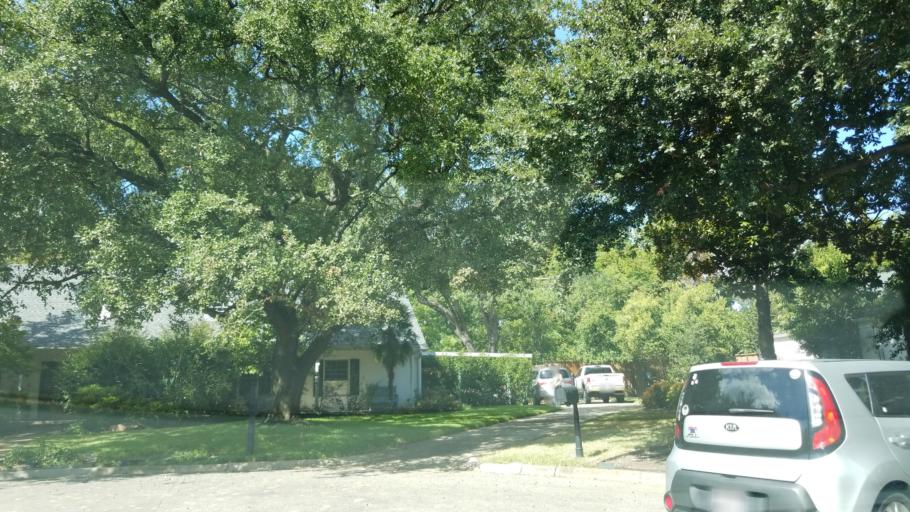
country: US
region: Texas
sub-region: Dallas County
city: Addison
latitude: 32.9321
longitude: -96.7980
